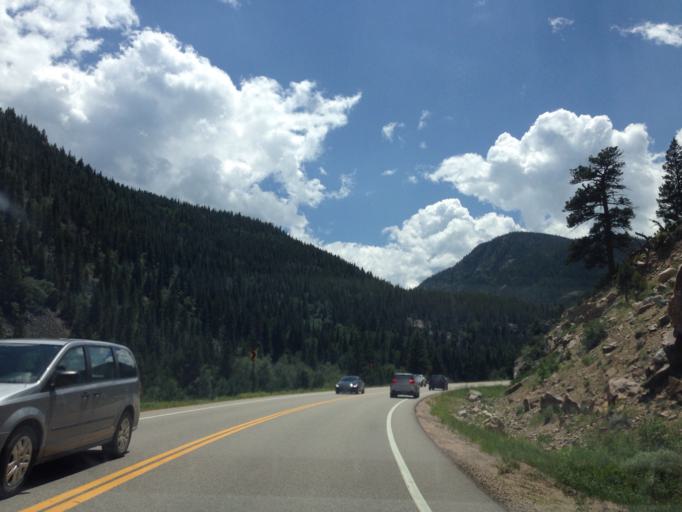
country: US
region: Colorado
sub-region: Larimer County
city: Estes Park
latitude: 40.6625
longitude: -105.8101
